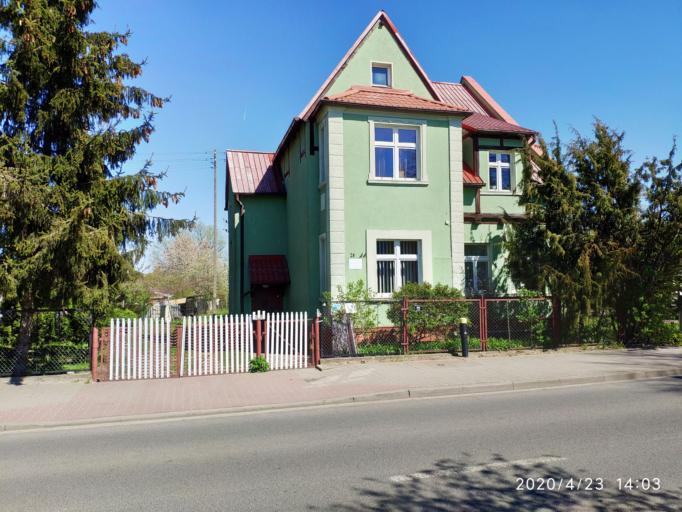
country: PL
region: Lubusz
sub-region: Powiat slubicki
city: Osno Lubuskie
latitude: 52.4512
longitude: 14.8783
